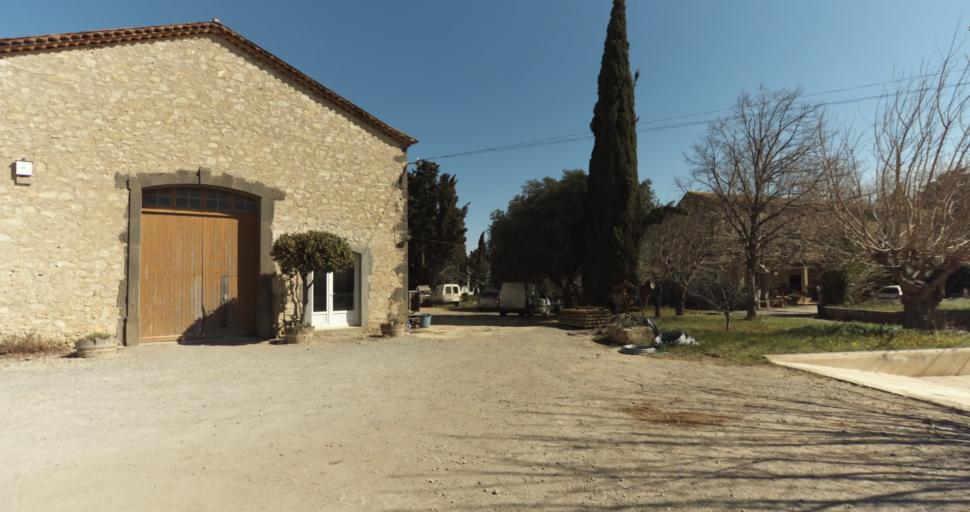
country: FR
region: Languedoc-Roussillon
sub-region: Departement de l'Herault
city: Marseillan
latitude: 43.3757
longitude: 3.5409
